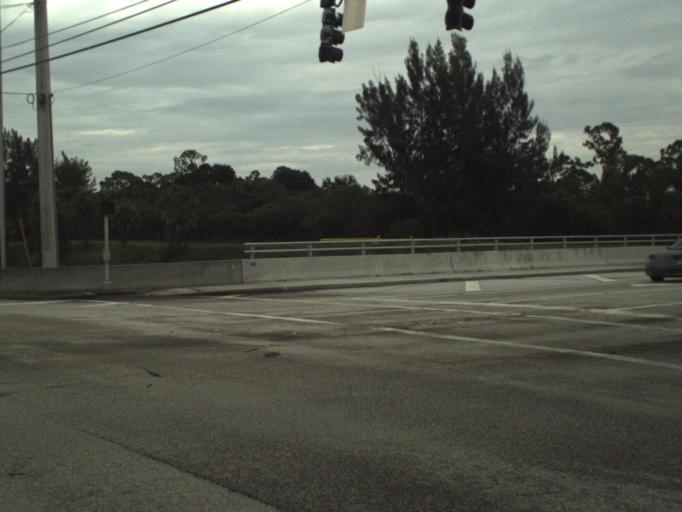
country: US
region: Florida
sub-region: Palm Beach County
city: Loxahatchee Groves
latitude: 26.6819
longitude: -80.2588
